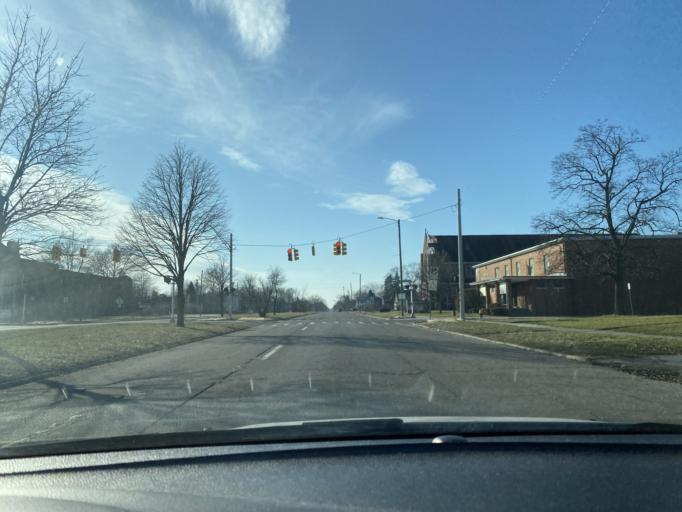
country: US
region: Michigan
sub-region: Wayne County
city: Grosse Pointe Park
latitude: 42.4058
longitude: -82.9475
